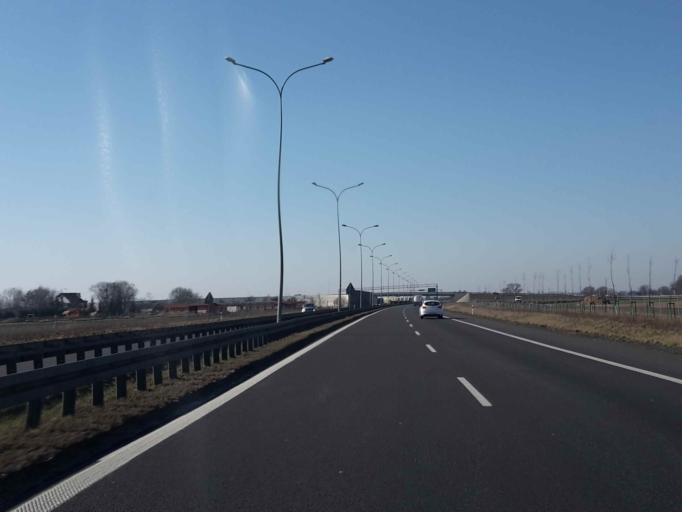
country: PL
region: Greater Poland Voivodeship
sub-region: Powiat poznanski
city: Kleszczewo
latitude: 52.3434
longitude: 17.1691
